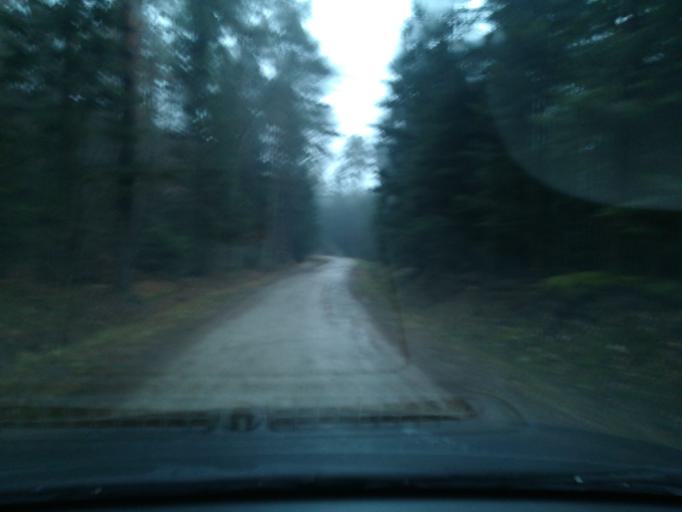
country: PL
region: Subcarpathian Voivodeship
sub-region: Powiat lancucki
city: Bialobrzegi
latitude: 50.1251
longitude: 22.3652
